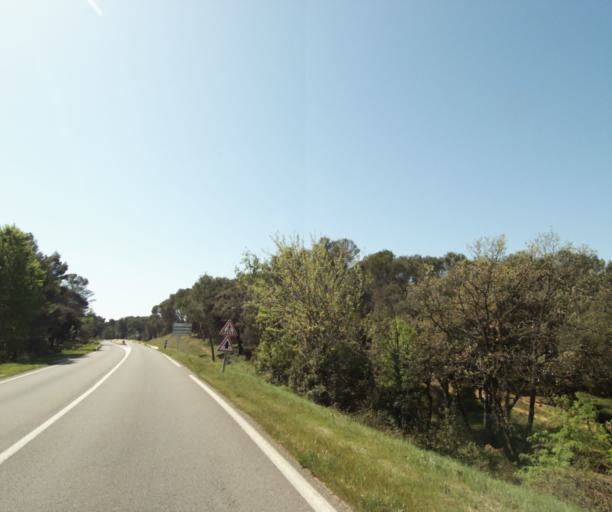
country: FR
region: Languedoc-Roussillon
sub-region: Departement de l'Herault
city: Clapiers
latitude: 43.6535
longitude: 3.8977
